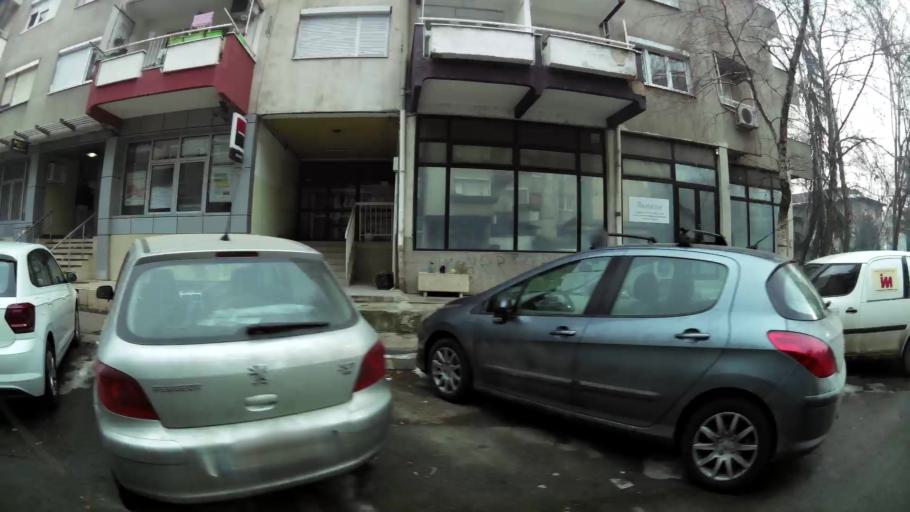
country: MK
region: Cair
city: Cair
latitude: 42.0037
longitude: 21.4618
